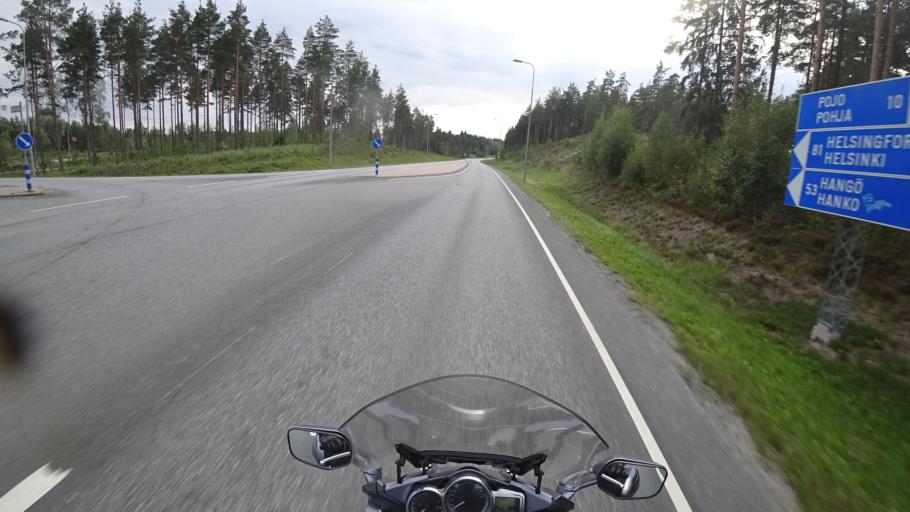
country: FI
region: Uusimaa
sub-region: Raaseporin
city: Karis
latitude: 60.0738
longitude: 23.6514
